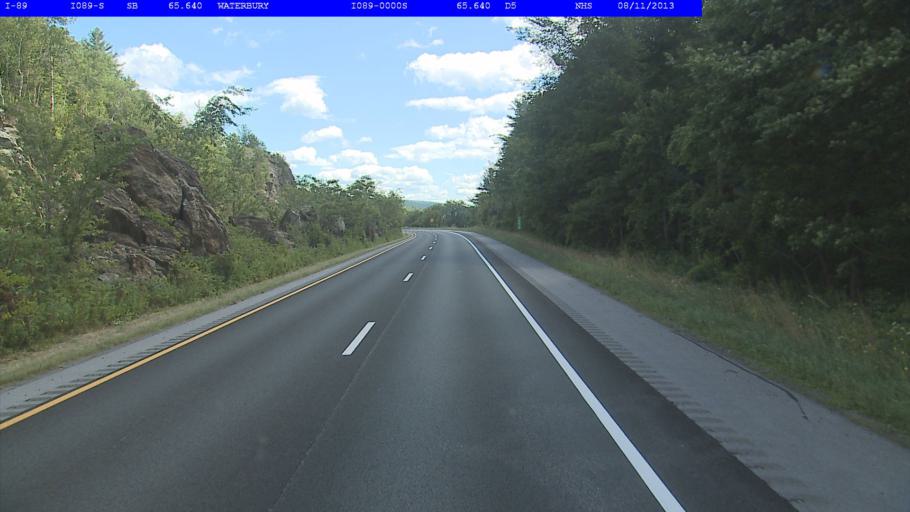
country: US
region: Vermont
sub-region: Washington County
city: Waterbury
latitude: 44.3543
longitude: -72.7855
